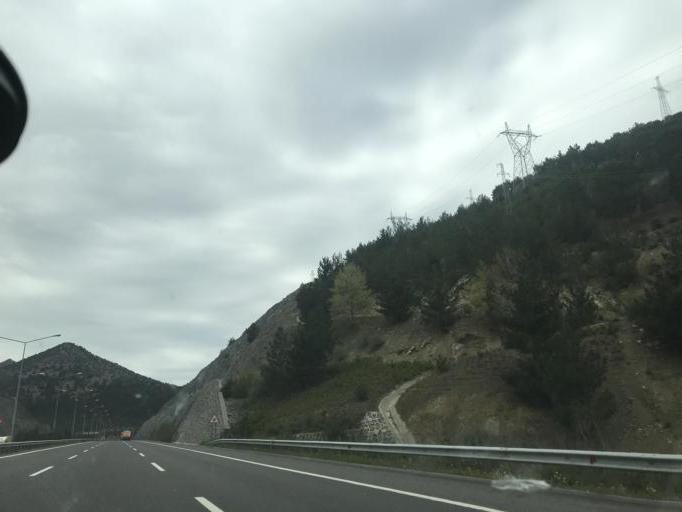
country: TR
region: Nigde
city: Ciftehan
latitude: 37.4992
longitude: 34.8272
